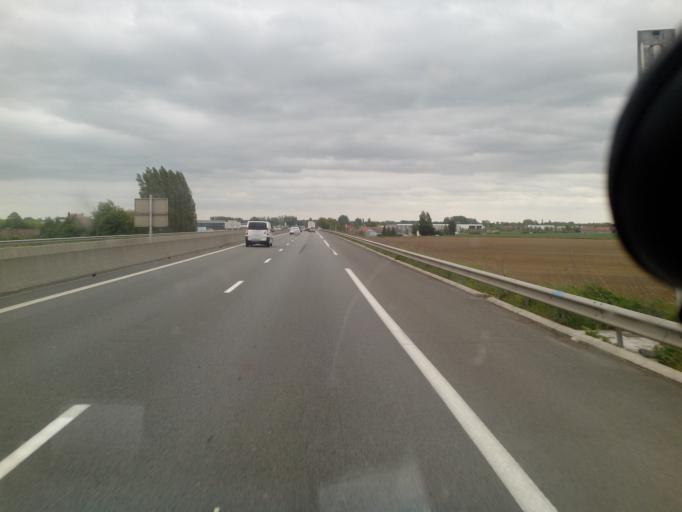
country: FR
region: Nord-Pas-de-Calais
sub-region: Departement du Nord
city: Bailleul
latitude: 50.7256
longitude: 2.7268
